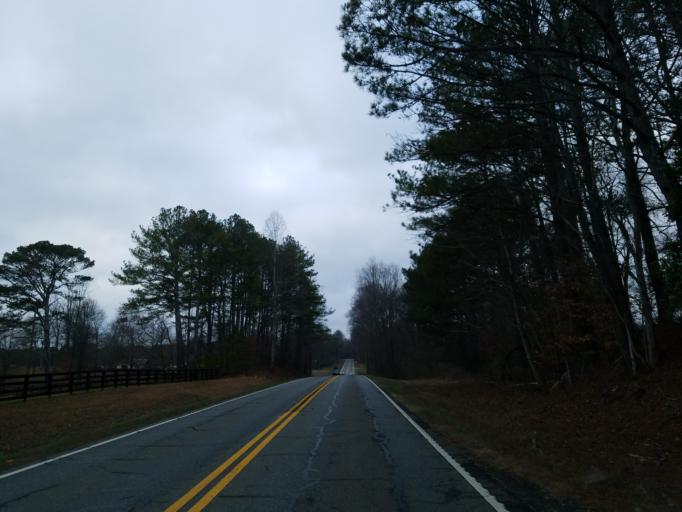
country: US
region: Georgia
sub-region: Cherokee County
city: Canton
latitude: 34.3318
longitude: -84.5634
